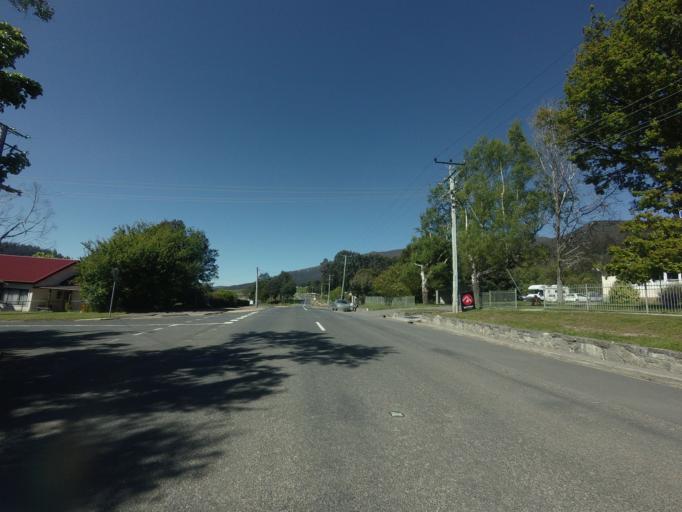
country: AU
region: Tasmania
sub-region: Derwent Valley
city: New Norfolk
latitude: -42.7548
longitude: 146.6280
